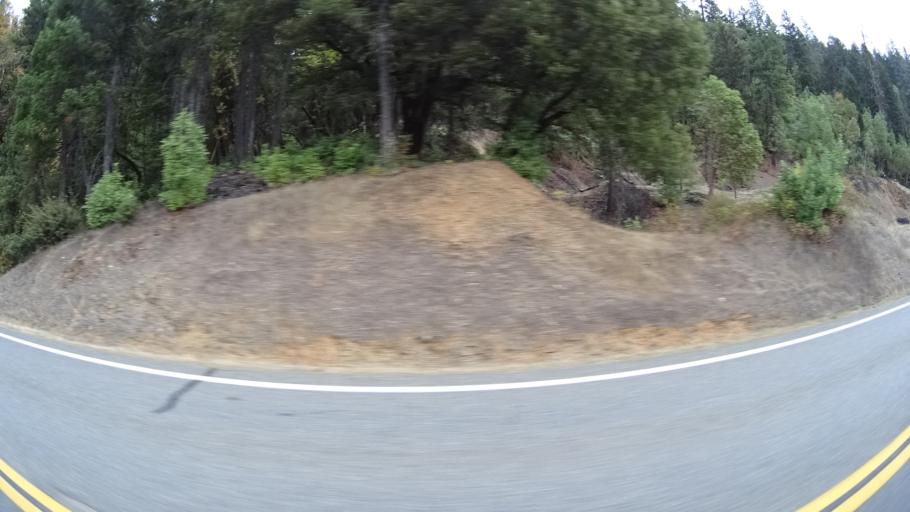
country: US
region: California
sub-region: Siskiyou County
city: Happy Camp
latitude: 41.8114
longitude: -123.3549
